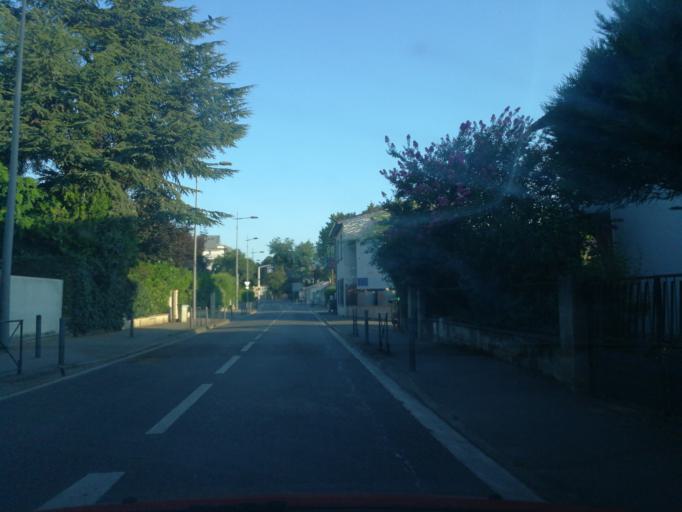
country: FR
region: Midi-Pyrenees
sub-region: Departement de la Haute-Garonne
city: Balma
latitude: 43.6096
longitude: 1.4798
